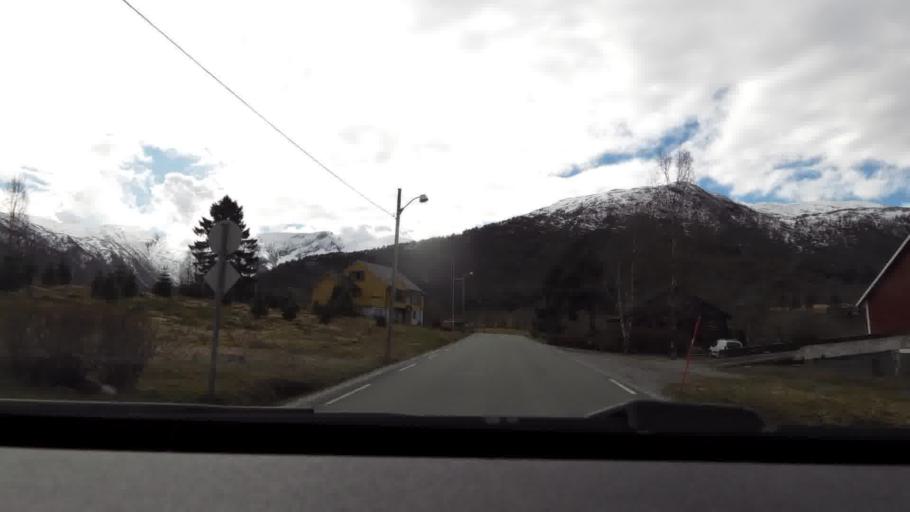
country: NO
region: More og Romsdal
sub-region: Eide
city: Eide
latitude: 62.9113
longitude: 7.5406
